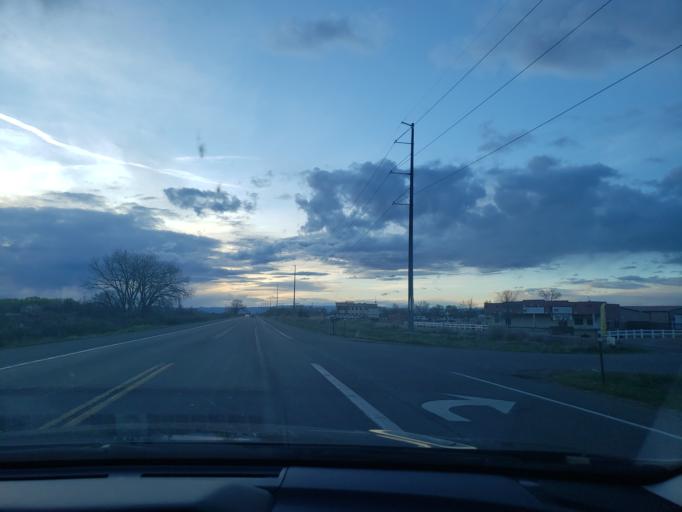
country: US
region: Colorado
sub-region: Mesa County
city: Fruita
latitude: 39.1326
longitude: -108.6887
